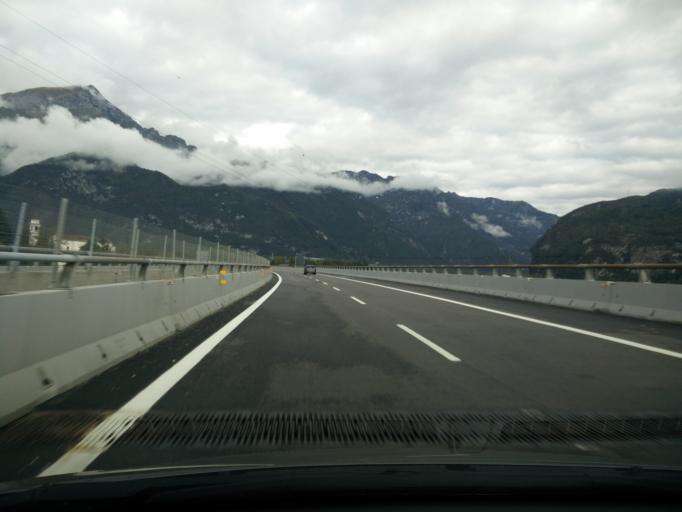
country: IT
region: Veneto
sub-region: Provincia di Belluno
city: Soccher-Paiane-Casan-Arsie
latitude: 46.1721
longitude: 12.3081
